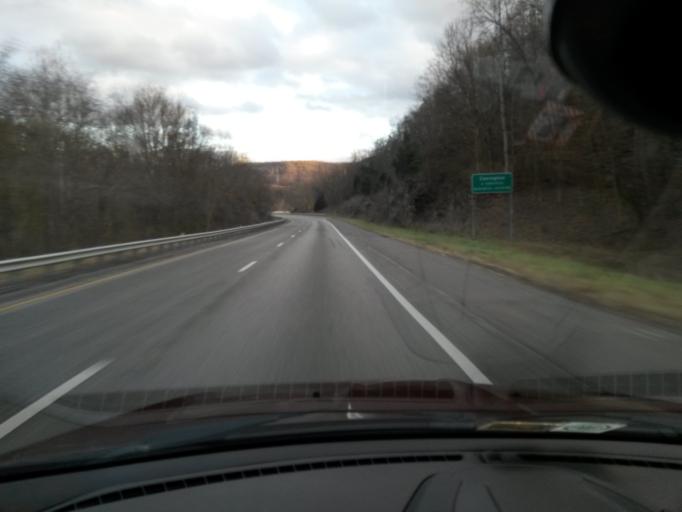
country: US
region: Virginia
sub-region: City of Covington
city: Fairlawn
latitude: 37.7754
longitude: -79.9990
